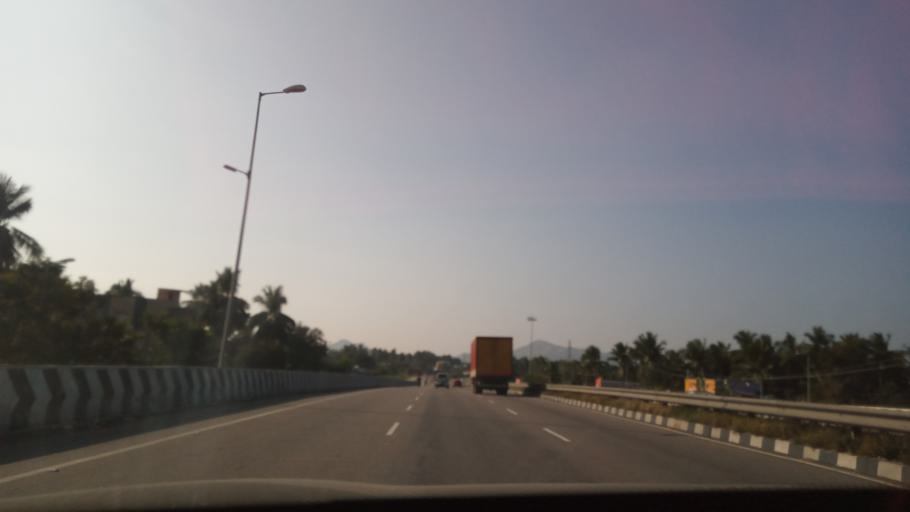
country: IN
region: Tamil Nadu
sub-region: Krishnagiri
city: Krishnagiri
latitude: 12.5757
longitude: 78.1676
